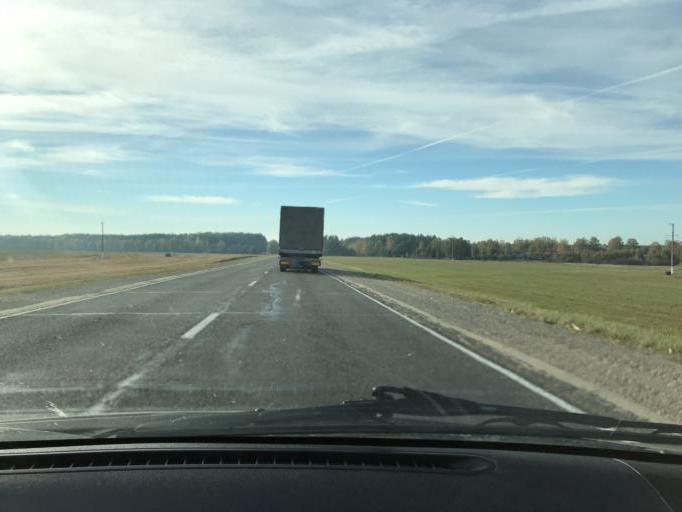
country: BY
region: Brest
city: Horad Pinsk
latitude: 52.1501
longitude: 25.8622
